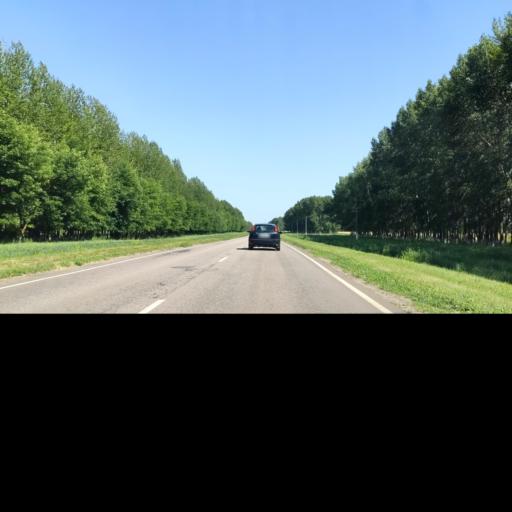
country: RU
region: Voronezj
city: Panino
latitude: 51.6650
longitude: 39.9732
